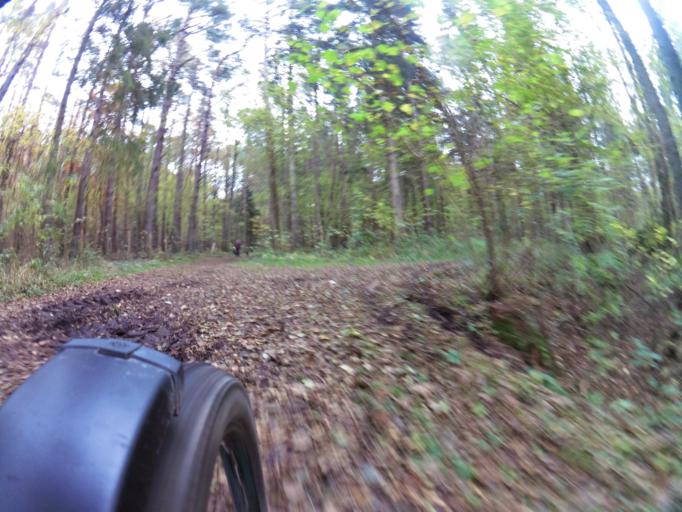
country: PL
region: Pomeranian Voivodeship
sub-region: Powiat pucki
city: Krokowa
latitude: 54.8309
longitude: 18.1081
